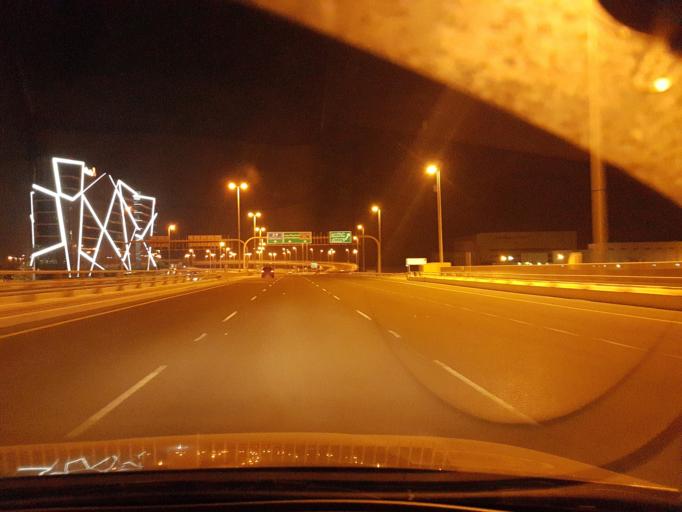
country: BH
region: Muharraq
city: Al Muharraq
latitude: 26.2503
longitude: 50.5856
